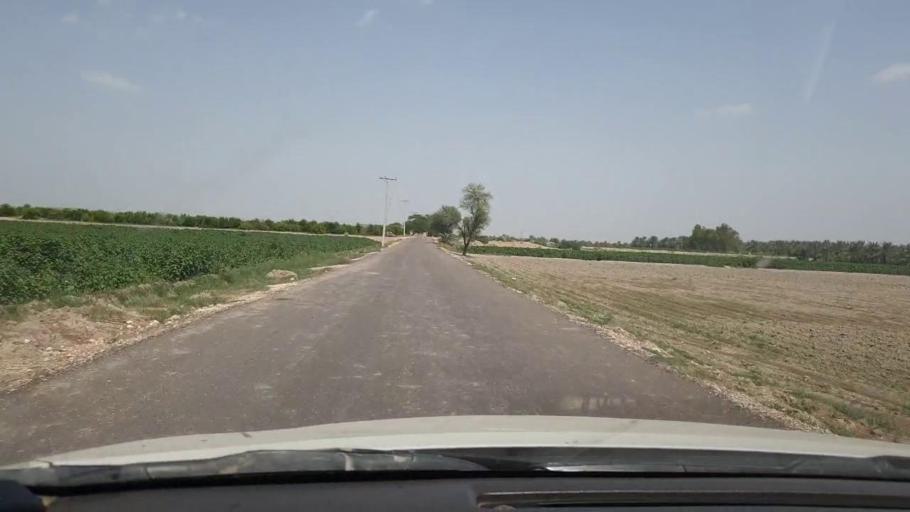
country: PK
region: Sindh
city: Rohri
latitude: 27.4821
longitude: 69.0662
